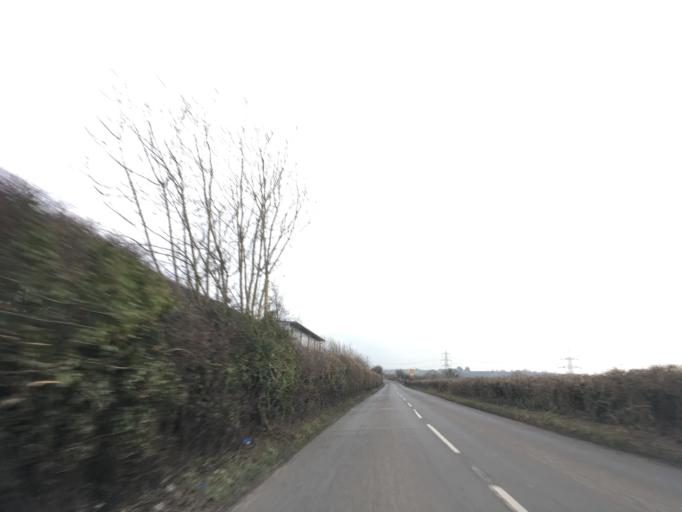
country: GB
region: England
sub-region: South Gloucestershire
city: Yate
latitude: 51.5330
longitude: -2.4388
